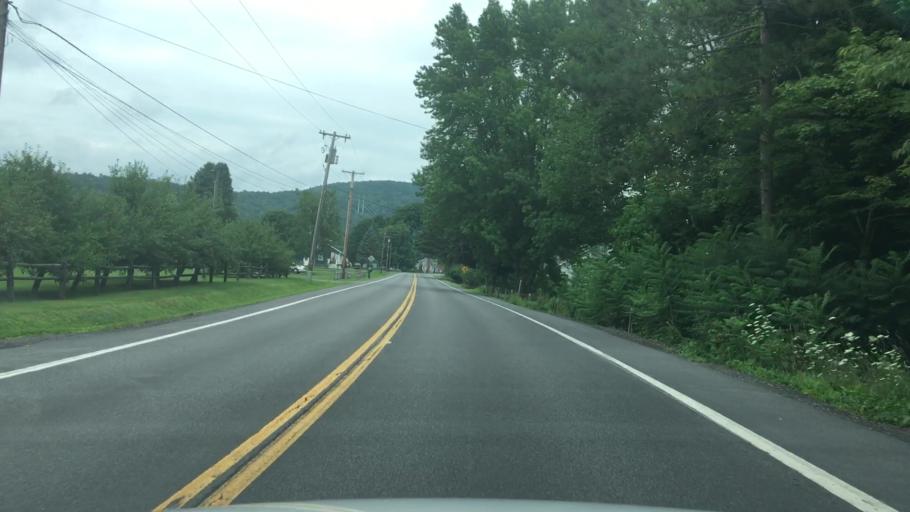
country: US
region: New York
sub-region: Otsego County
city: Otego
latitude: 42.4185
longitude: -75.1435
